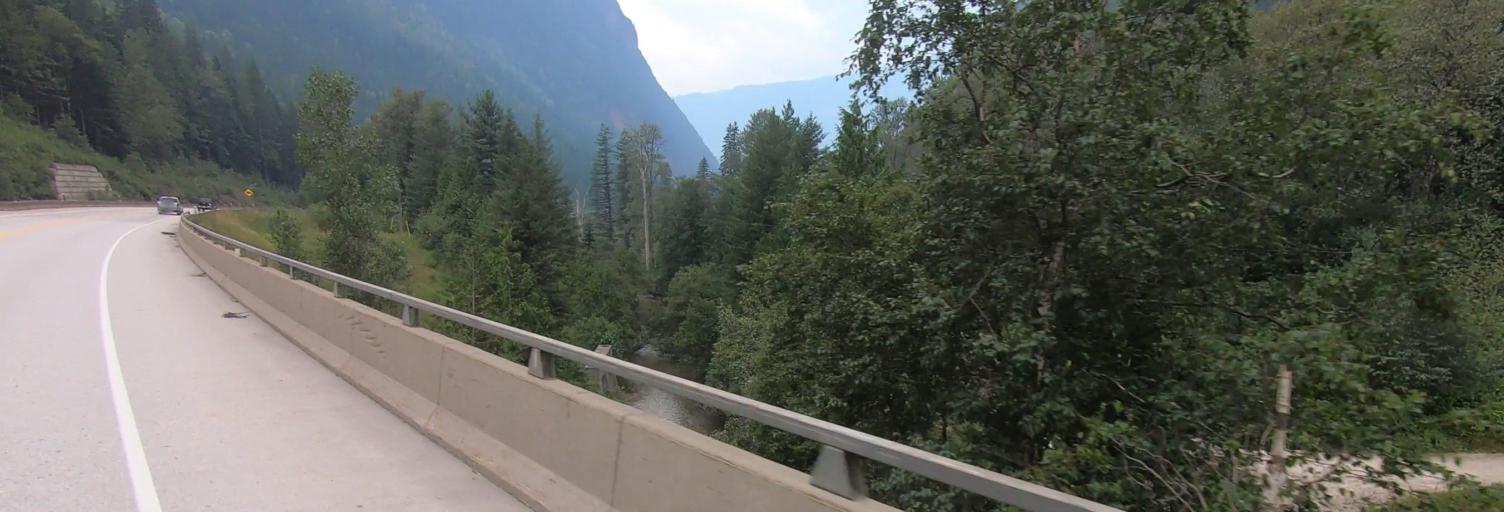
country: CA
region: British Columbia
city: Revelstoke
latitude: 50.9399
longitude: -118.4276
